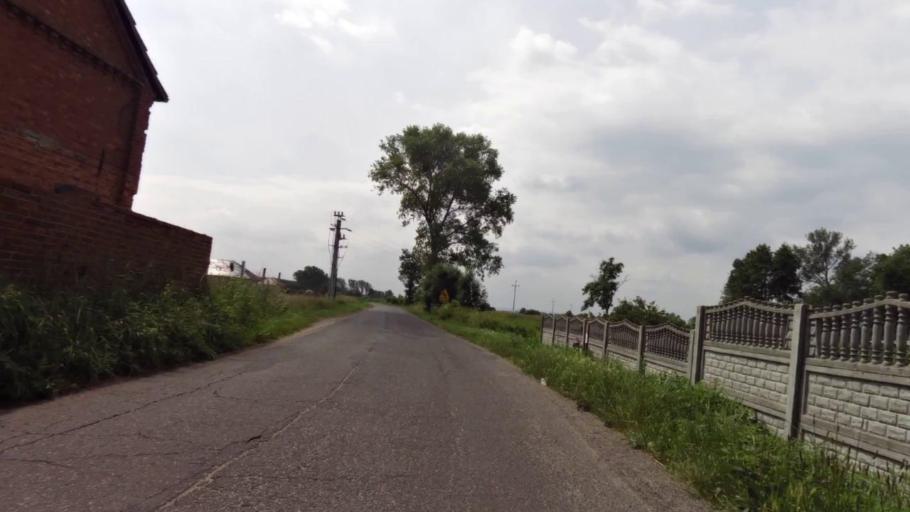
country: PL
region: West Pomeranian Voivodeship
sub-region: Powiat goleniowski
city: Goleniow
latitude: 53.5030
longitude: 14.7089
